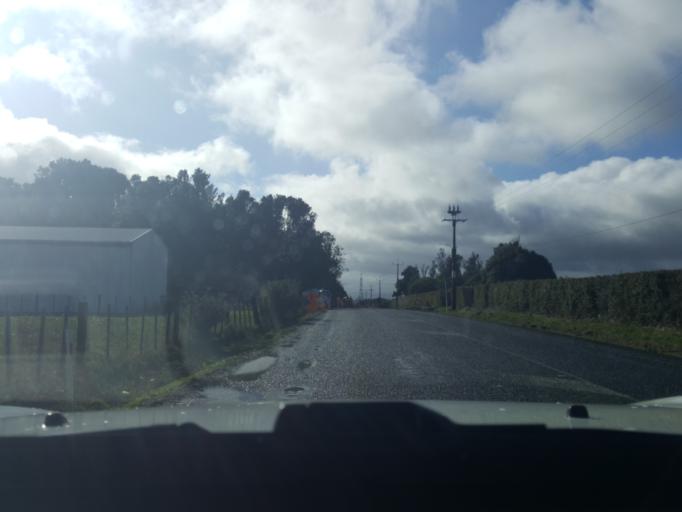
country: NZ
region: Auckland
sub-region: Auckland
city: Pukekohe East
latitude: -37.3099
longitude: 174.9877
